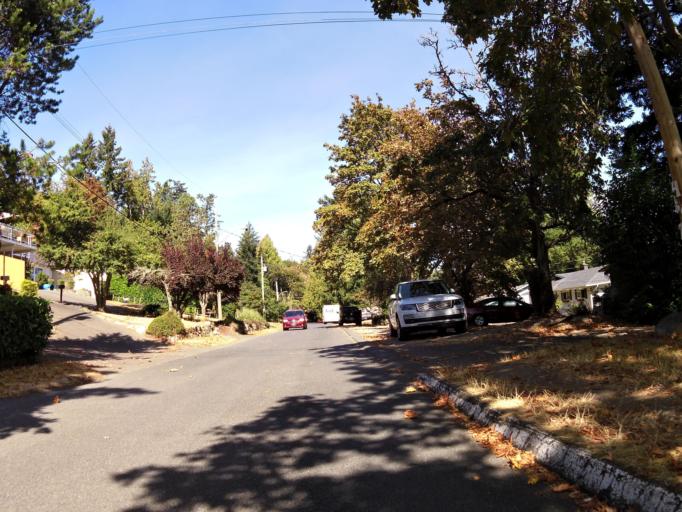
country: CA
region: British Columbia
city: Victoria
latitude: 48.5108
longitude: -123.3662
